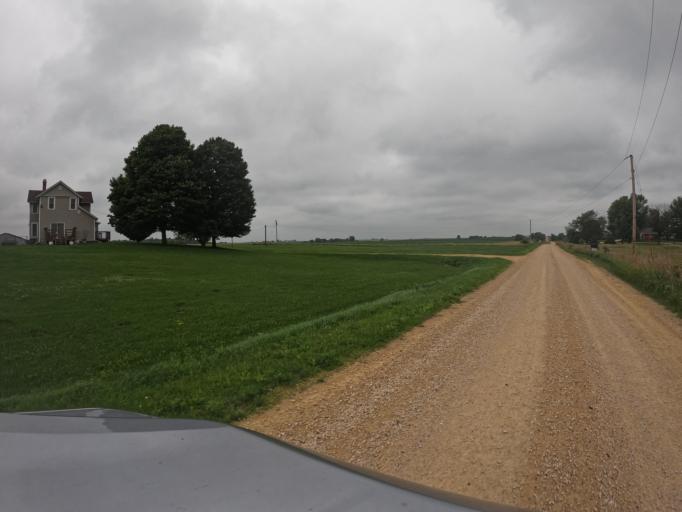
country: US
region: Iowa
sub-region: Clinton County
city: De Witt
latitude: 41.8946
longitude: -90.5925
